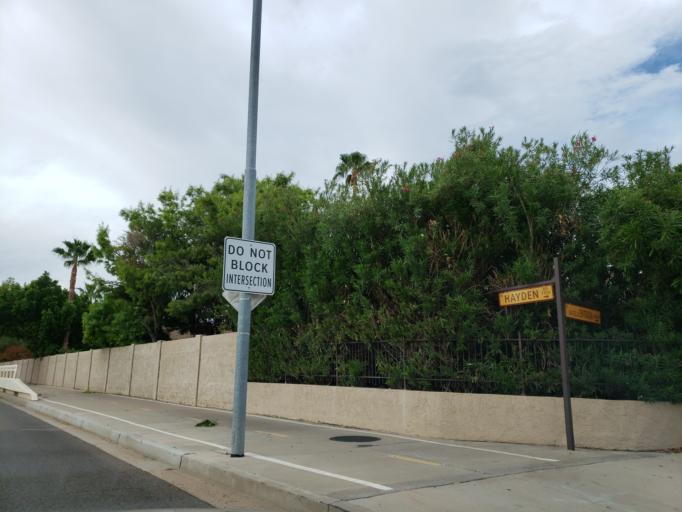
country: US
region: Arizona
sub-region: Maricopa County
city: Scottsdale
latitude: 33.5401
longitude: -111.9088
